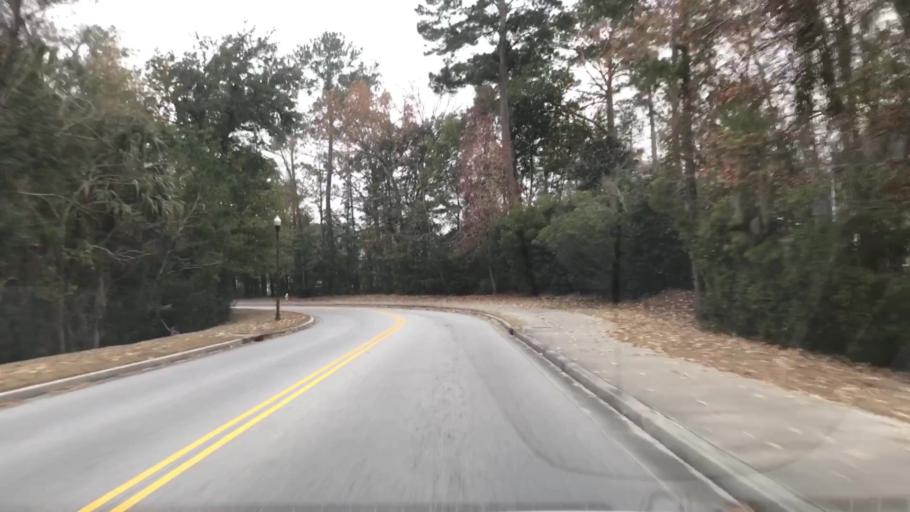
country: US
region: South Carolina
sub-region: Charleston County
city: Shell Point
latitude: 32.8010
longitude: -80.0809
